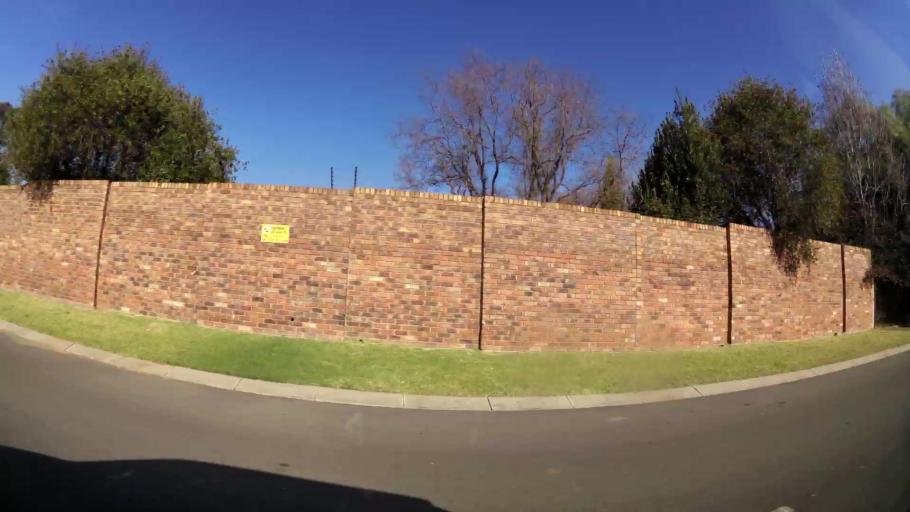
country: ZA
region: Gauteng
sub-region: City of Johannesburg Metropolitan Municipality
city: Johannesburg
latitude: -26.1737
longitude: 28.1162
